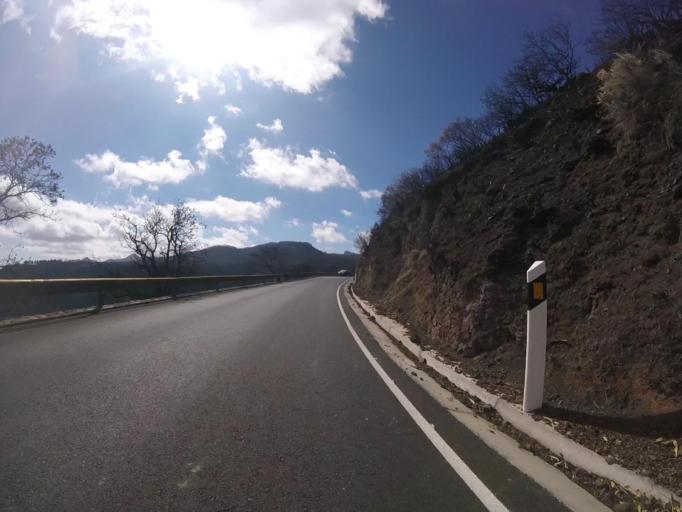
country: ES
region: Canary Islands
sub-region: Provincia de Las Palmas
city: Tejeda
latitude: 27.9961
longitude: -15.5946
